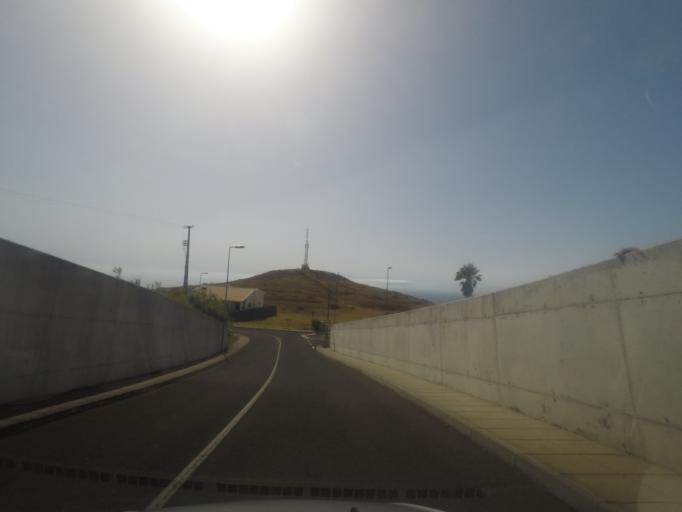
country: PT
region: Madeira
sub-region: Calheta
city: Faja da Ovelha
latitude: 32.8155
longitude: -17.2536
